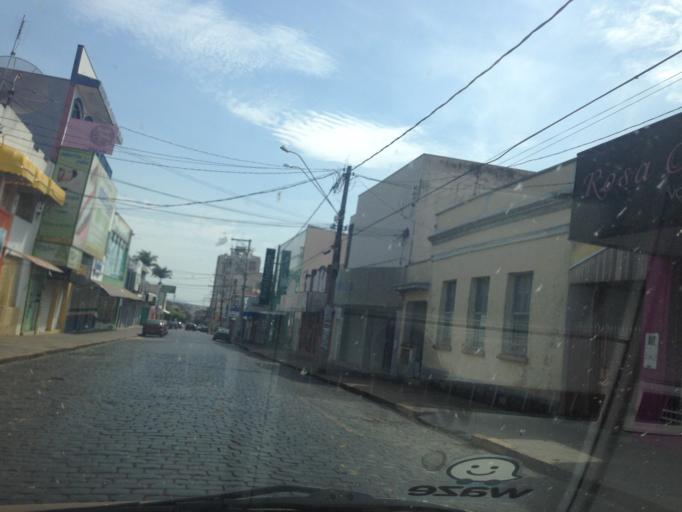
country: BR
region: Sao Paulo
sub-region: Casa Branca
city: Casa Branca
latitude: -21.7744
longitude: -47.0838
